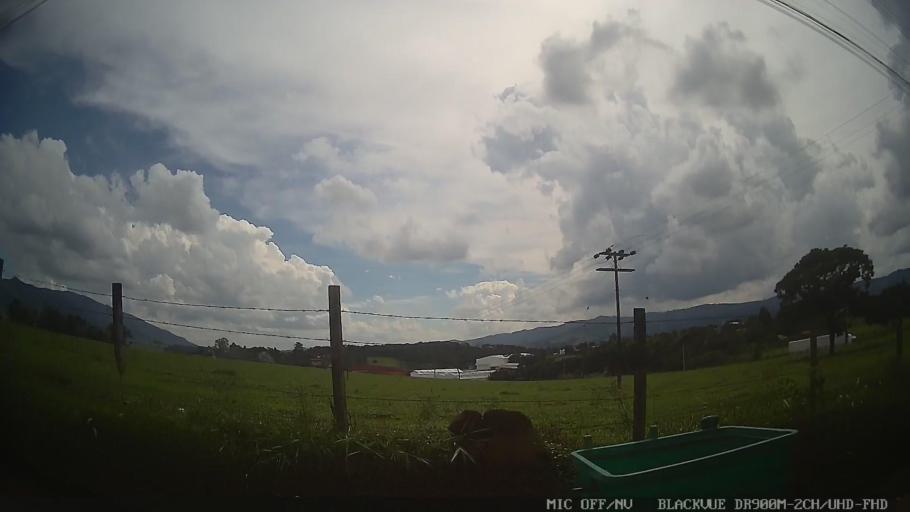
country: BR
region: Minas Gerais
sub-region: Extrema
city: Extrema
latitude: -22.8228
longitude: -46.2864
